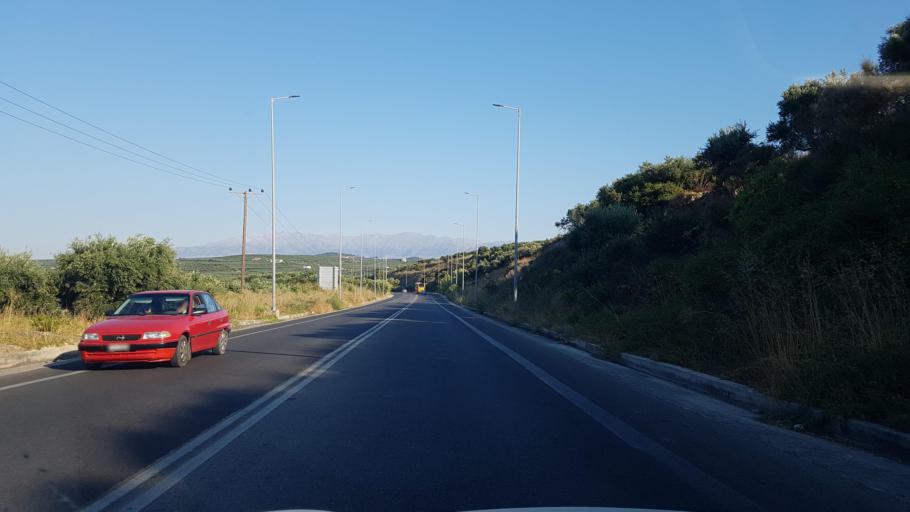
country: GR
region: Crete
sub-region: Nomos Chanias
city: Kolympari
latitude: 35.5329
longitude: 23.7782
